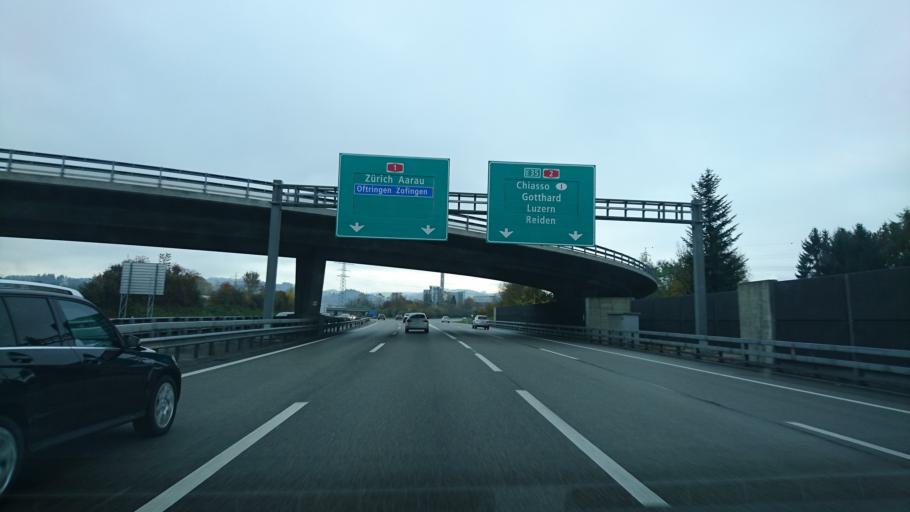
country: CH
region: Aargau
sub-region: Bezirk Zofingen
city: Oftringen
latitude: 47.3049
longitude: 7.9141
